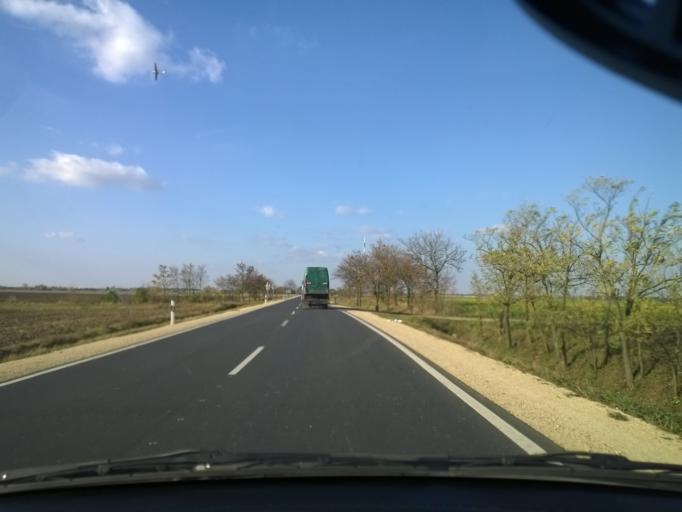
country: HU
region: Csongrad
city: Szentes
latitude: 46.6069
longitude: 20.2920
